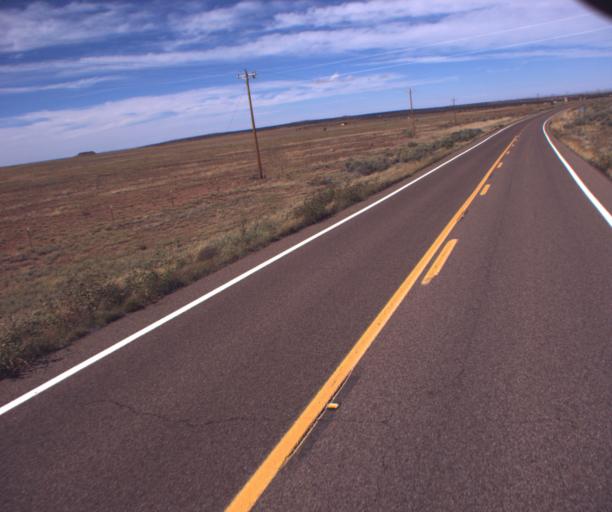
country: US
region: Arizona
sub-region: Apache County
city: Saint Johns
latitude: 34.4923
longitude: -109.6210
